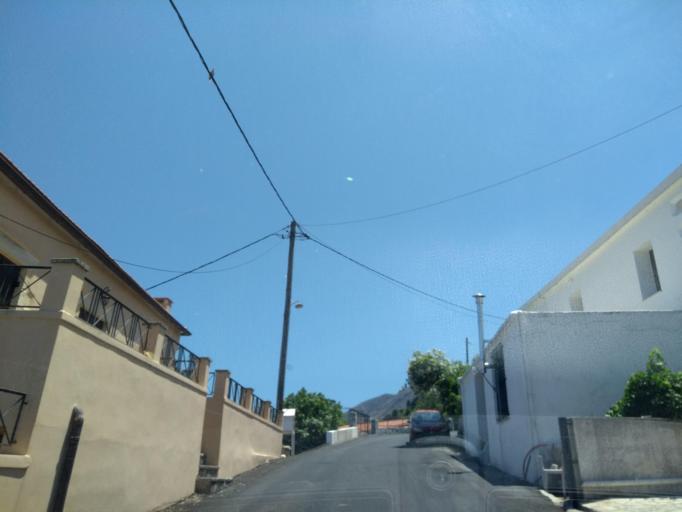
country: GR
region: Crete
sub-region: Nomos Chanias
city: Georgioupolis
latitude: 35.3177
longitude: 24.3095
